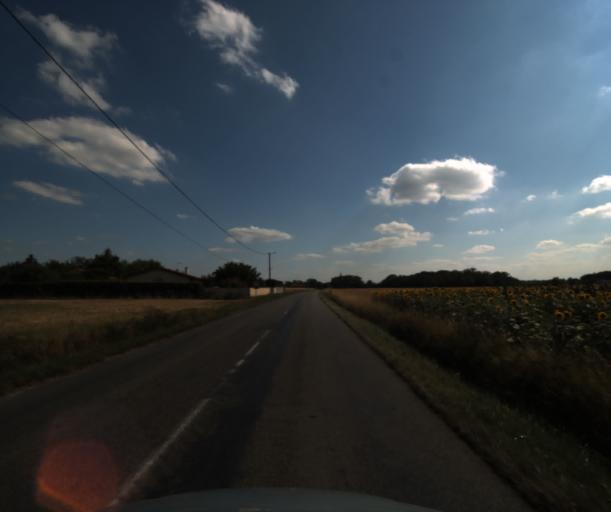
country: FR
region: Midi-Pyrenees
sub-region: Departement de la Haute-Garonne
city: Saint-Lys
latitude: 43.5229
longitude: 1.1813
